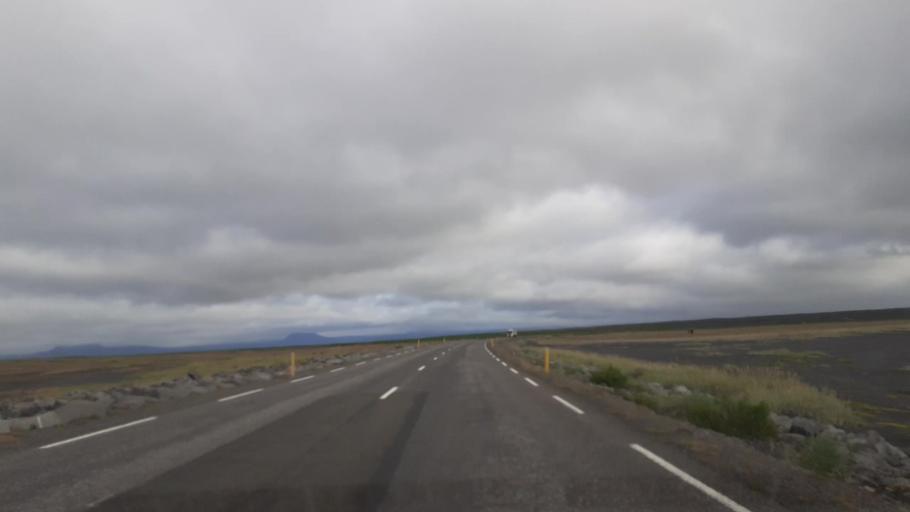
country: IS
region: Northeast
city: Husavik
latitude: 66.1196
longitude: -16.9241
